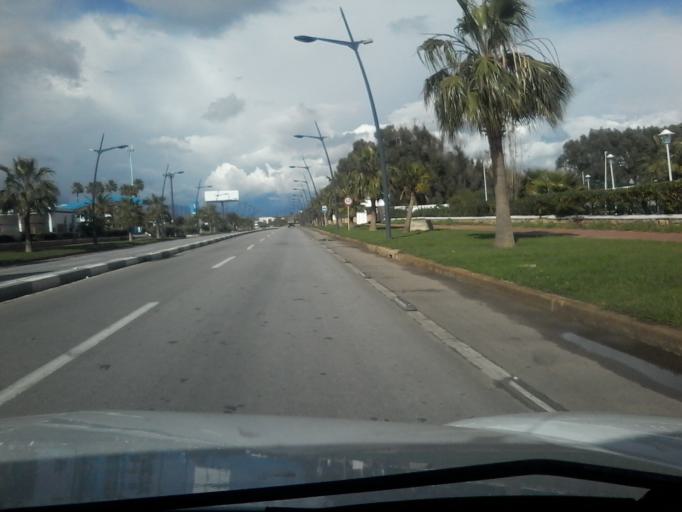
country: MA
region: Tanger-Tetouan
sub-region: Tetouan
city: Martil
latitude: 35.7349
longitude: -5.3417
